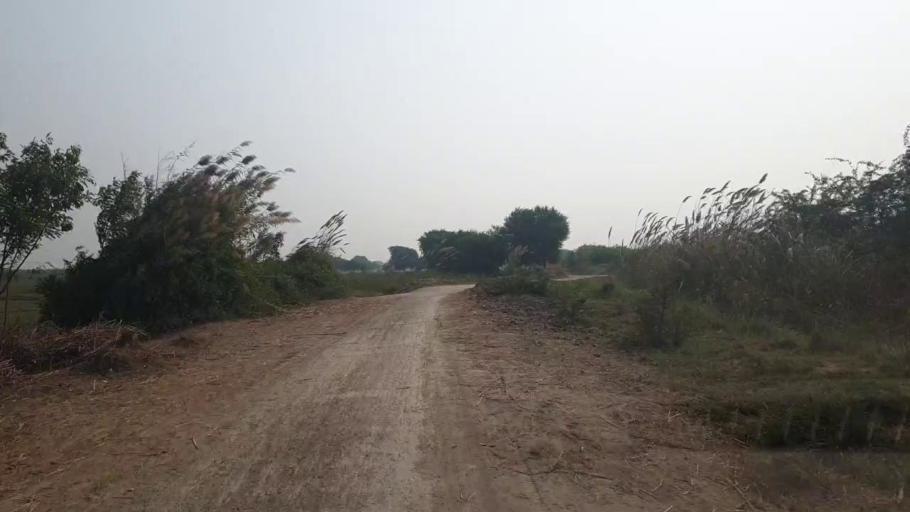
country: PK
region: Sindh
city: Tando Muhammad Khan
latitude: 25.2704
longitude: 68.4977
